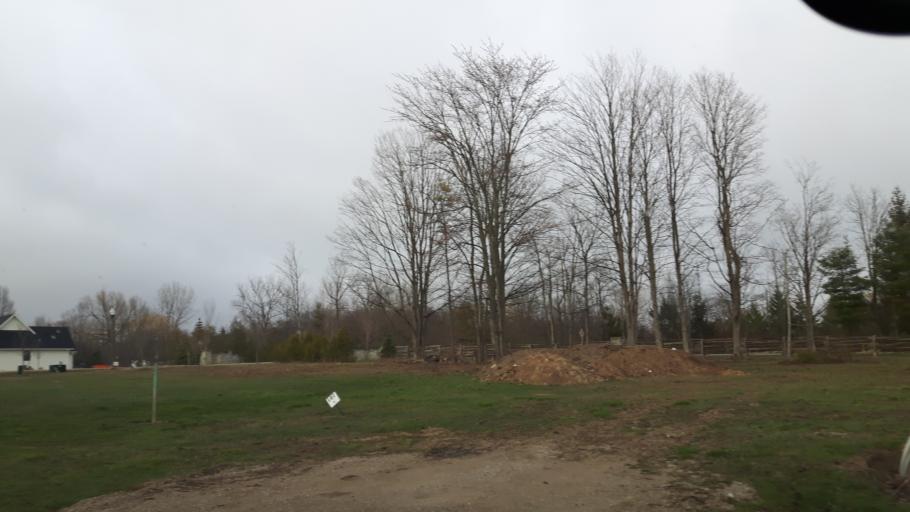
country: CA
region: Ontario
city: Bluewater
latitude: 43.5716
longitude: -81.7064
